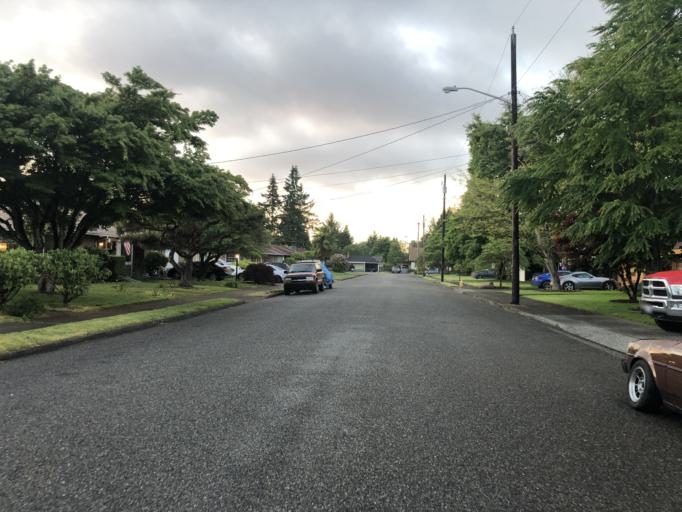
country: US
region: Washington
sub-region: King County
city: Auburn
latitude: 47.3120
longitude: -122.2096
